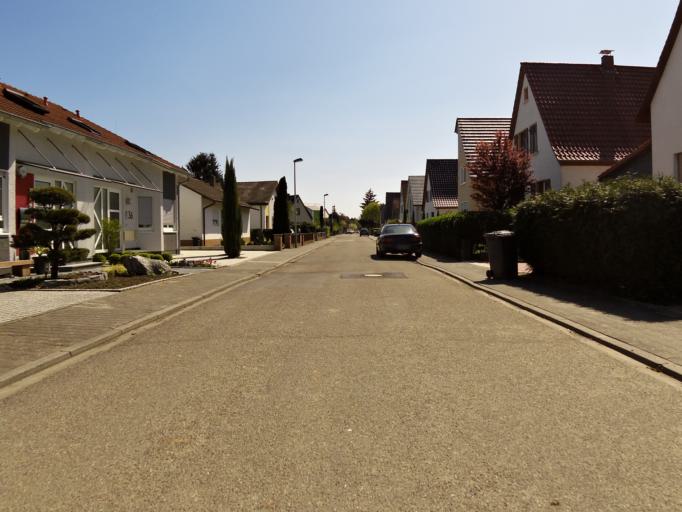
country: DE
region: Rheinland-Pfalz
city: Worms
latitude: 49.6372
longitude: 8.3877
